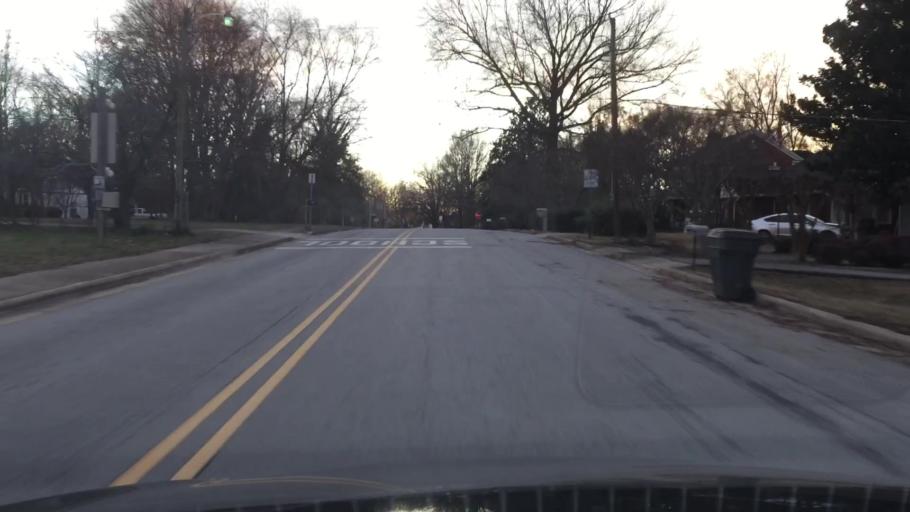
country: US
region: North Carolina
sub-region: Rockingham County
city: Reidsville
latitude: 36.3432
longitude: -79.6691
